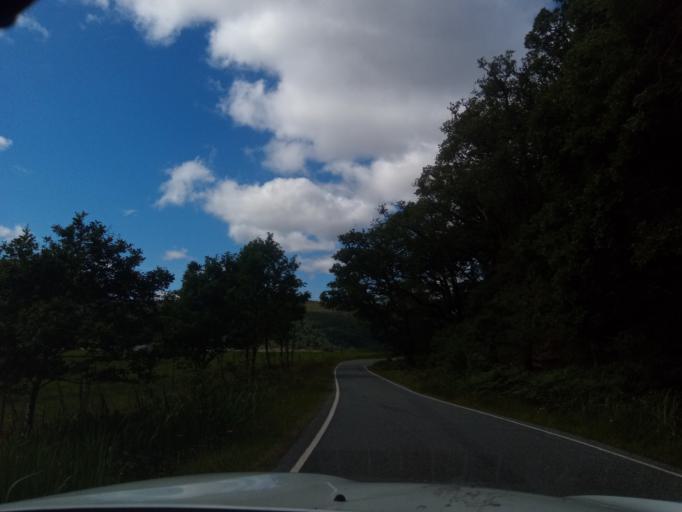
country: GB
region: Scotland
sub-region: Argyll and Bute
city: Isle Of Mull
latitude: 56.7907
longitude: -5.7633
